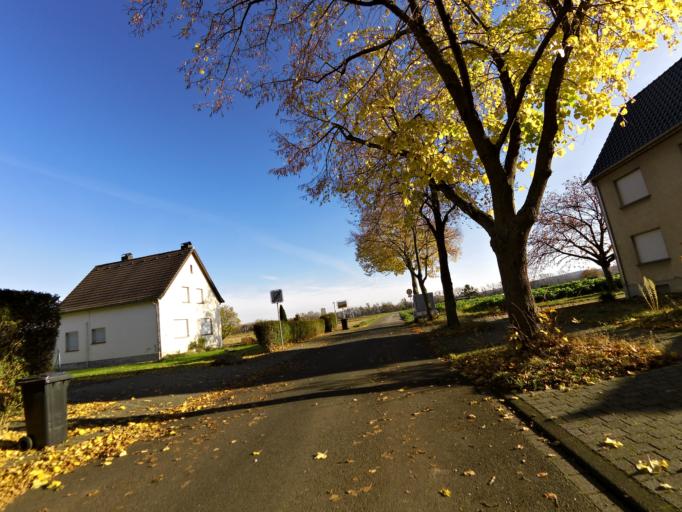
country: DE
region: North Rhine-Westphalia
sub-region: Regierungsbezirk Koln
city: Euskirchen
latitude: 50.6370
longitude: 6.8638
